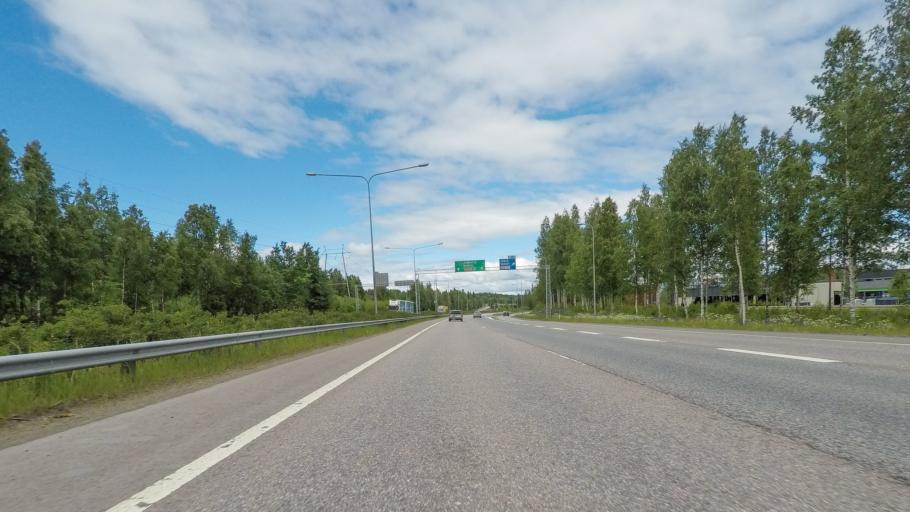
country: FI
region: Paijanne Tavastia
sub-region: Lahti
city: Lahti
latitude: 60.9804
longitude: 25.7317
